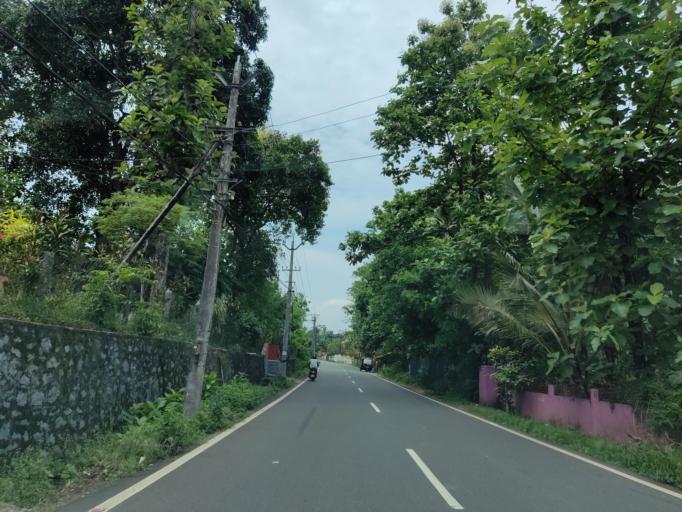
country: IN
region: Kerala
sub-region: Alappuzha
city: Chengannur
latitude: 9.2950
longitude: 76.6243
